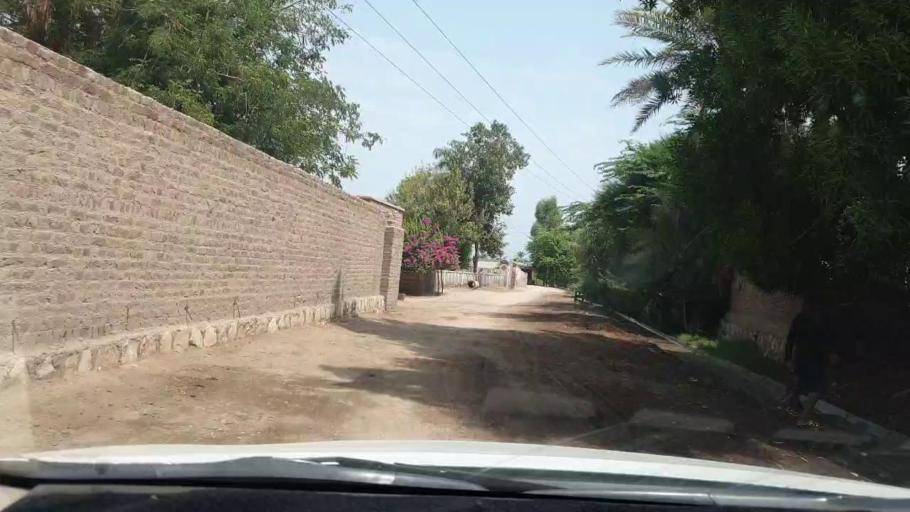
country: PK
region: Sindh
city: Rohri
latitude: 27.4965
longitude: 69.0236
